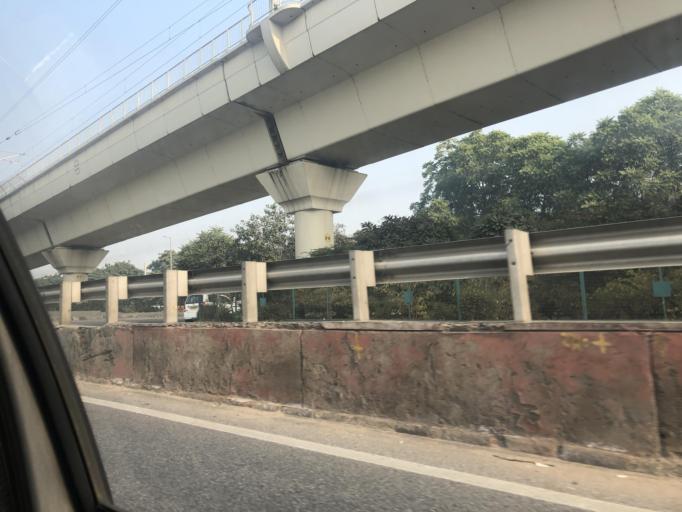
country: IN
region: NCT
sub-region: Central Delhi
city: Karol Bagh
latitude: 28.6105
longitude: 77.1388
